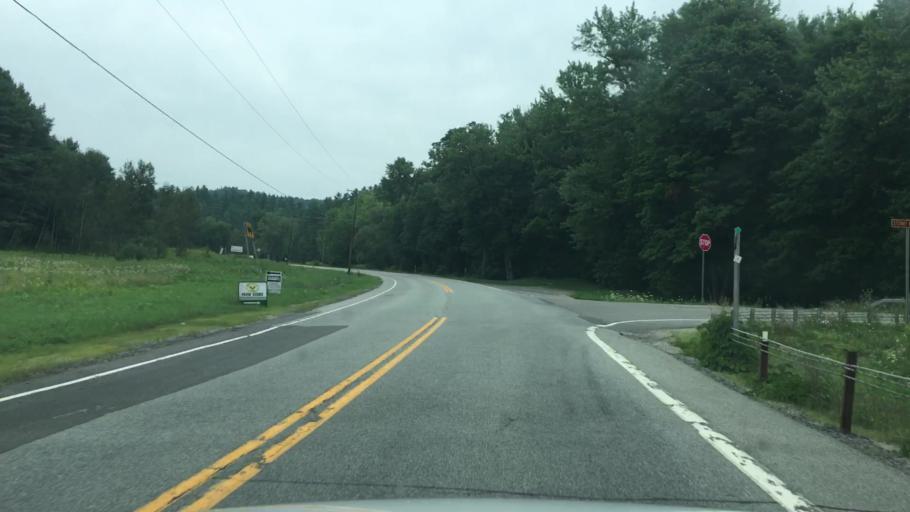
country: US
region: New York
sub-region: Essex County
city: Elizabethtown
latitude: 44.4130
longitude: -73.6816
